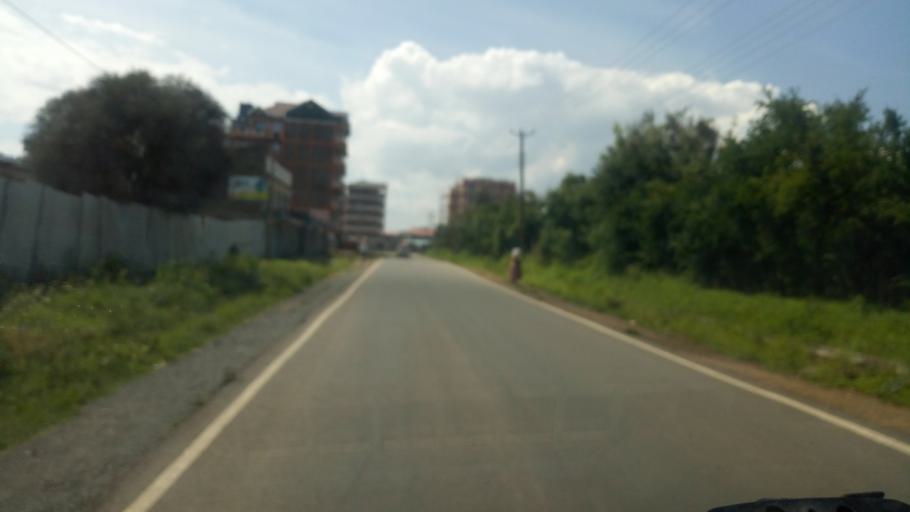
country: KE
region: Nakuru
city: Nakuru
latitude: -0.2794
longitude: 36.1022
